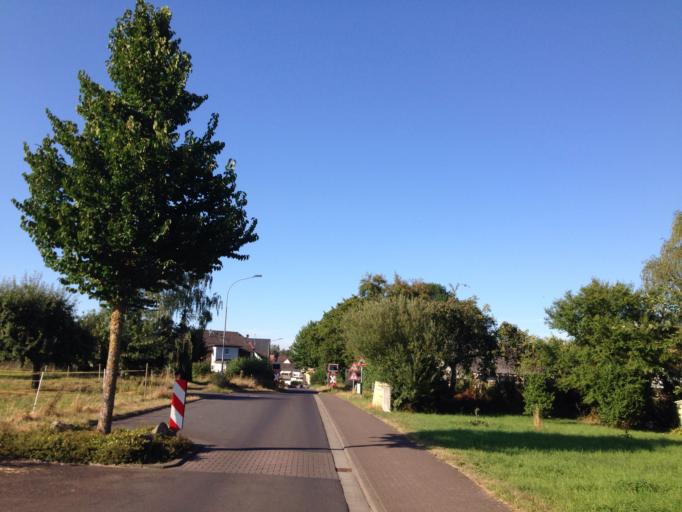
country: DE
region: Hesse
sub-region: Regierungsbezirk Giessen
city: Lich
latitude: 50.5350
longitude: 8.7479
